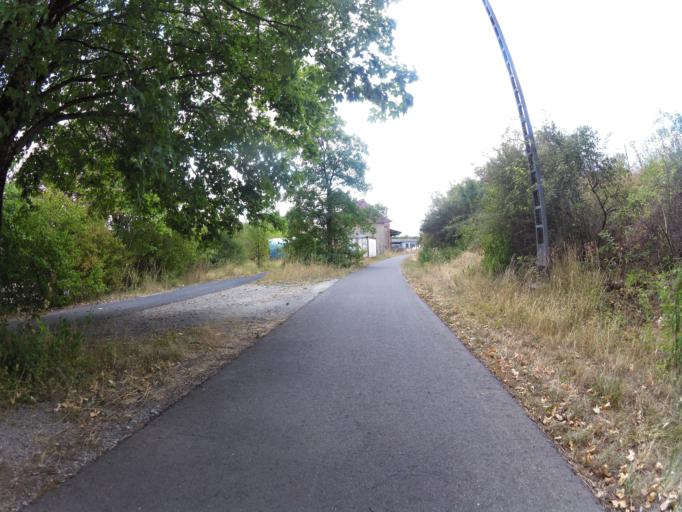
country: DE
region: Bavaria
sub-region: Regierungsbezirk Unterfranken
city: Aub
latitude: 49.5516
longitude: 10.0527
